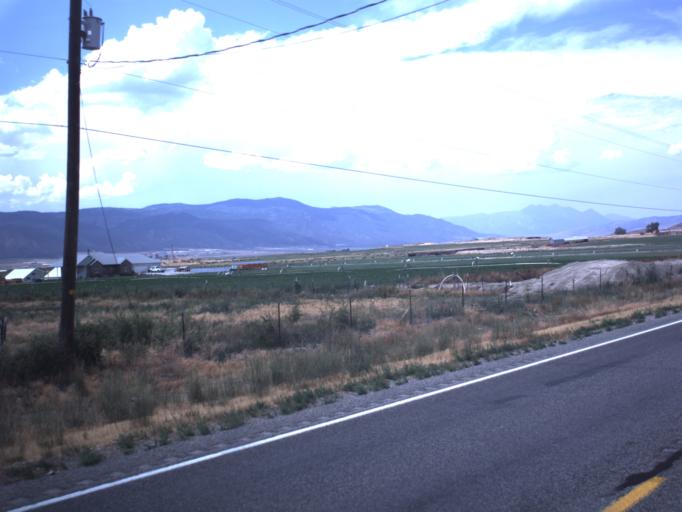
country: US
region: Utah
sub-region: Sanpete County
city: Moroni
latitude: 39.4877
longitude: -111.5630
